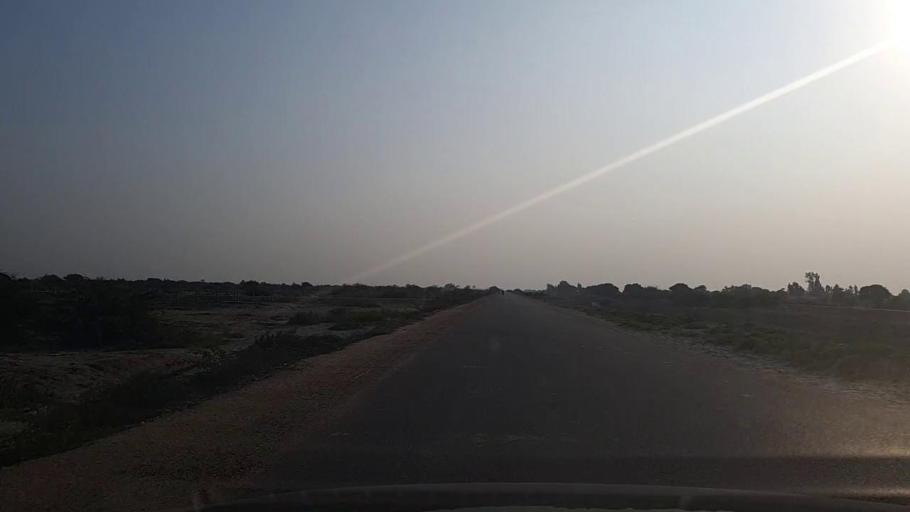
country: PK
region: Sindh
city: Mirpur Sakro
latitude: 24.4951
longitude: 67.8115
